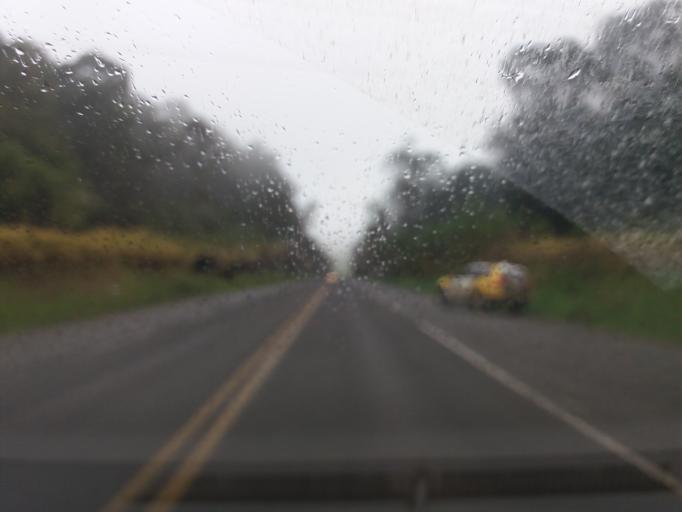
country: BR
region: Parana
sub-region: Francisco Beltrao
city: Francisco Beltrao
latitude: -26.0883
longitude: -53.2611
